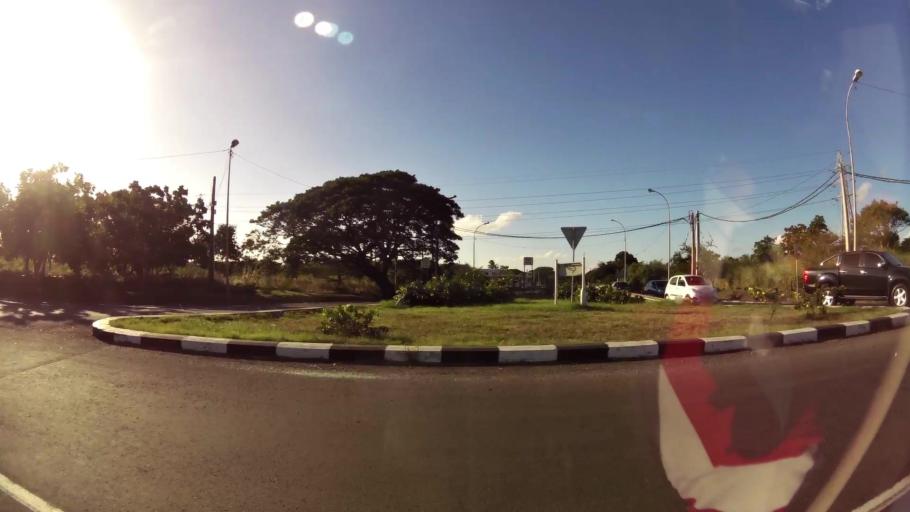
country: MU
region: Port Louis
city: Port Louis
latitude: -20.1522
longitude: 57.5055
